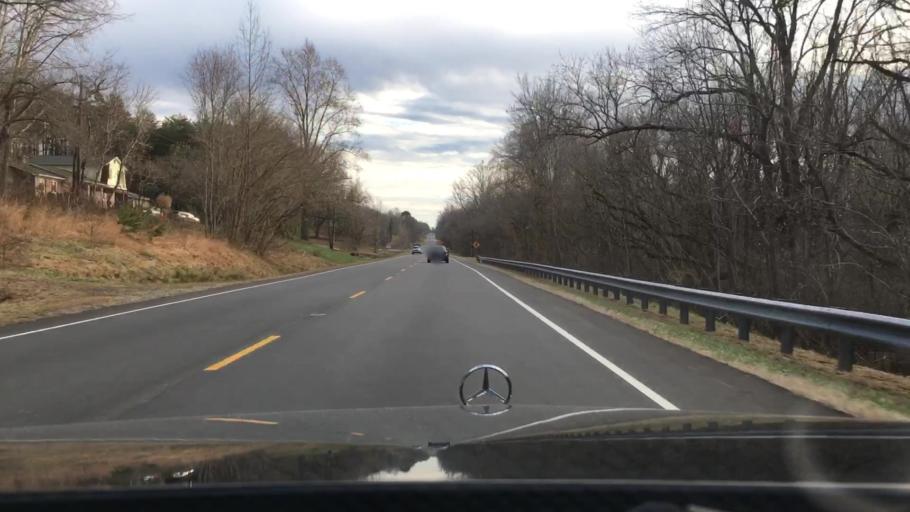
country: US
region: North Carolina
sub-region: Caswell County
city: Yanceyville
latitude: 36.4682
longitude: -79.3755
